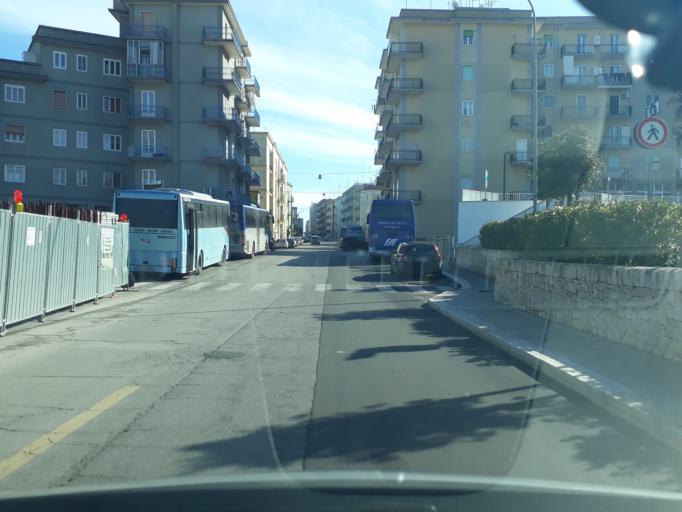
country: IT
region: Apulia
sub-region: Provincia di Taranto
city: Martina Franca
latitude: 40.7066
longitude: 17.3409
